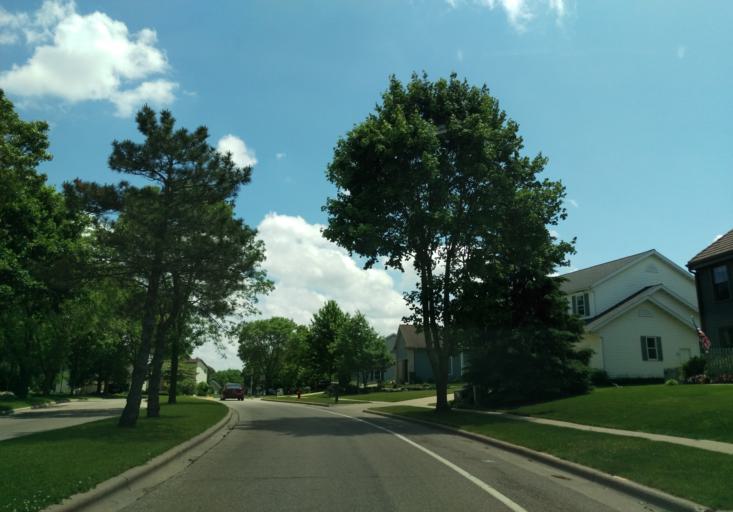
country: US
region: Wisconsin
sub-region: Dane County
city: Middleton
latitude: 43.0892
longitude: -89.5192
